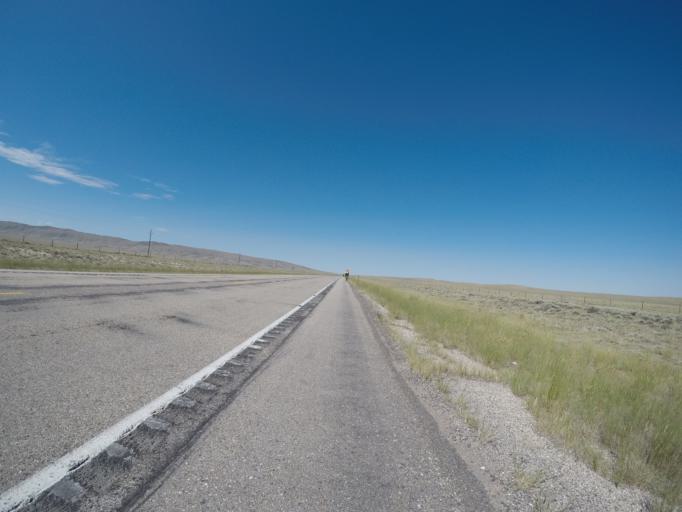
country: US
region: Wyoming
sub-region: Carbon County
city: Saratoga
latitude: 41.8103
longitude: -106.6828
